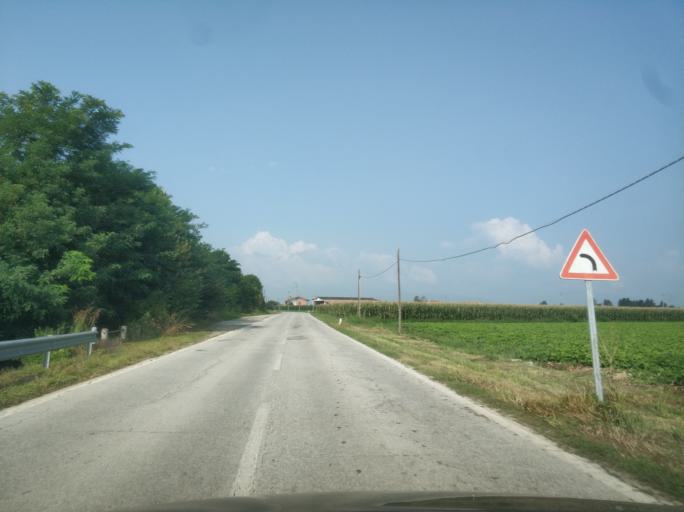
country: IT
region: Piedmont
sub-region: Provincia di Cuneo
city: Montanera
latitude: 44.5136
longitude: 7.6618
